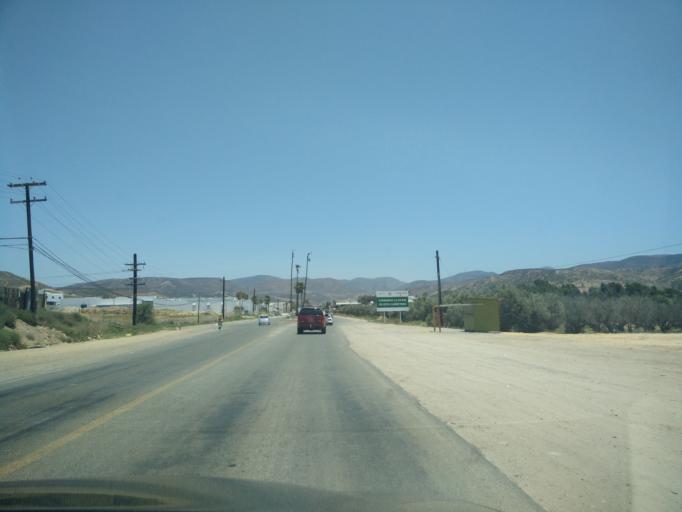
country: MX
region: Baja California
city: El Sauzal
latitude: 31.9034
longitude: -116.7019
